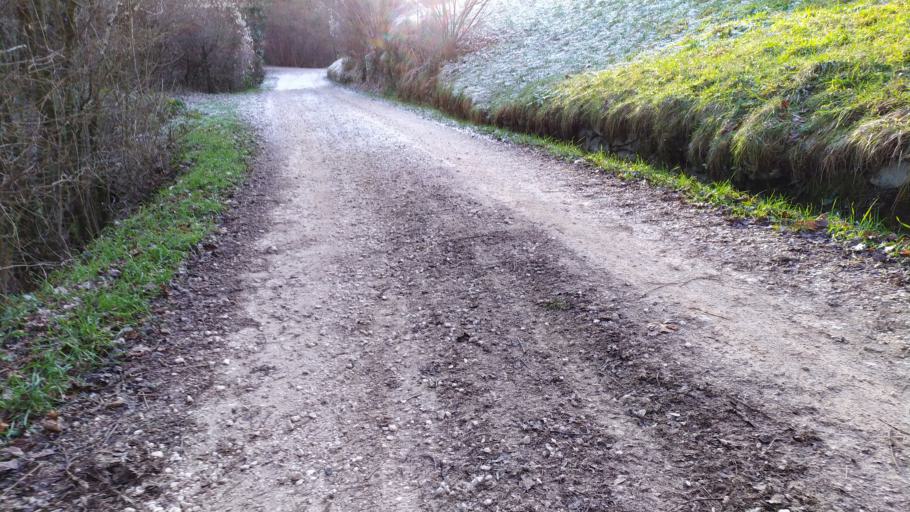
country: IT
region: Veneto
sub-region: Provincia di Vicenza
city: Monte di Malo
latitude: 45.6543
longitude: 11.3445
